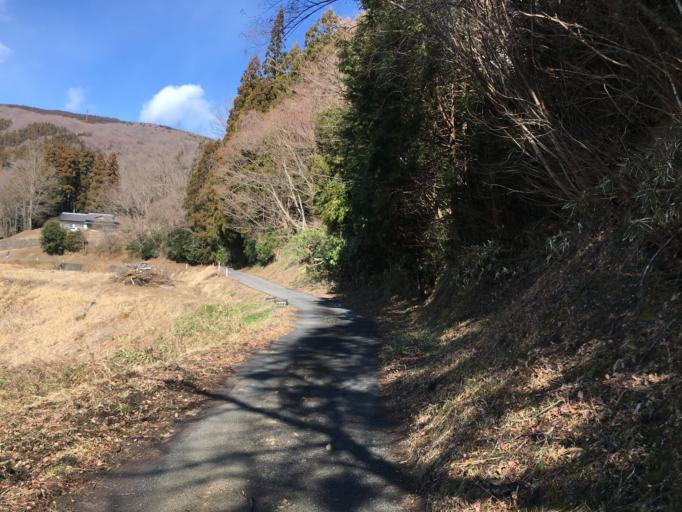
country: JP
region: Fukushima
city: Iwaki
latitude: 37.0045
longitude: 140.7964
